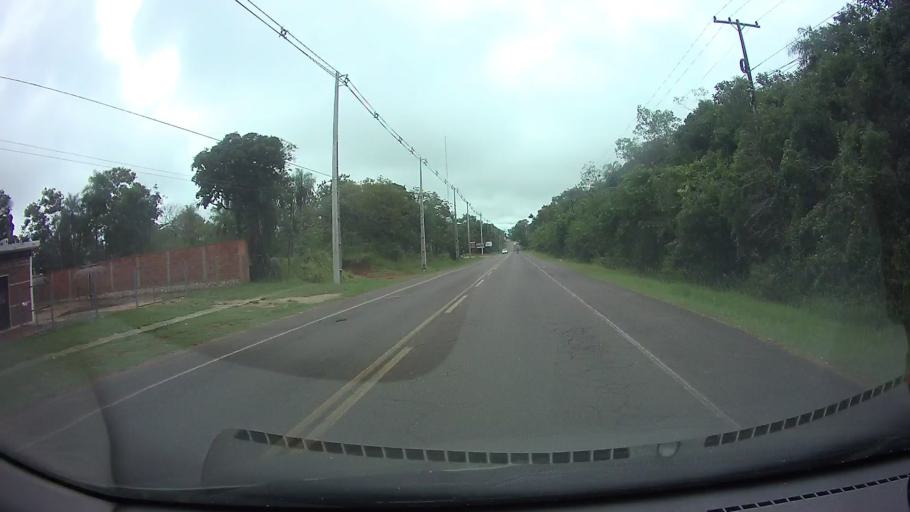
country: PY
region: Cordillera
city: Altos
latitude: -25.2798
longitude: -57.2615
